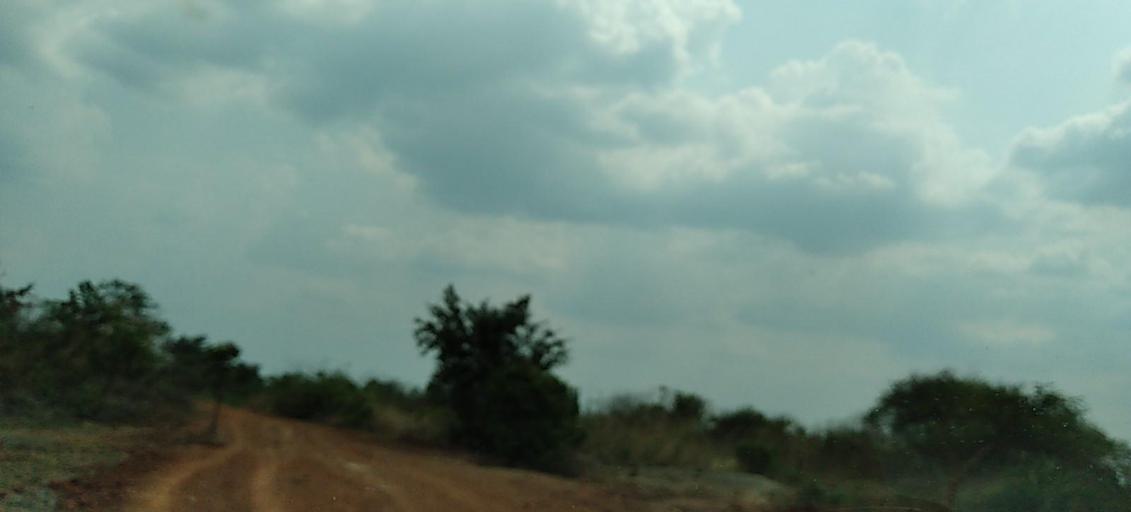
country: ZM
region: Copperbelt
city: Kalulushi
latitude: -12.8763
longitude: 28.0750
